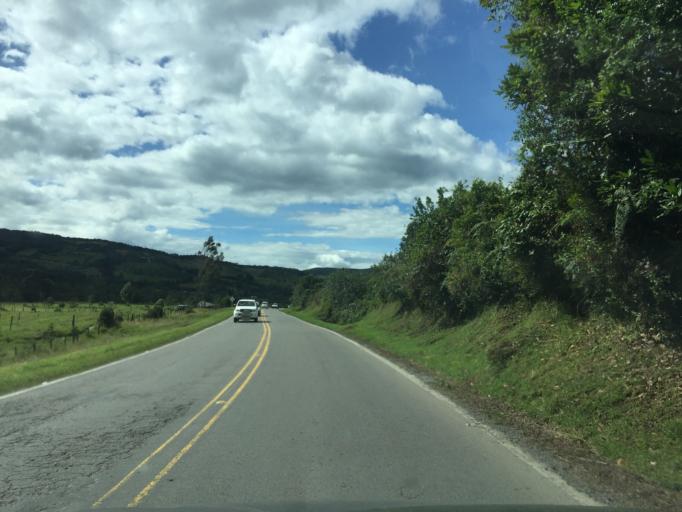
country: CO
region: Boyaca
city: Arcabuco
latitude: 5.7707
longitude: -73.4557
